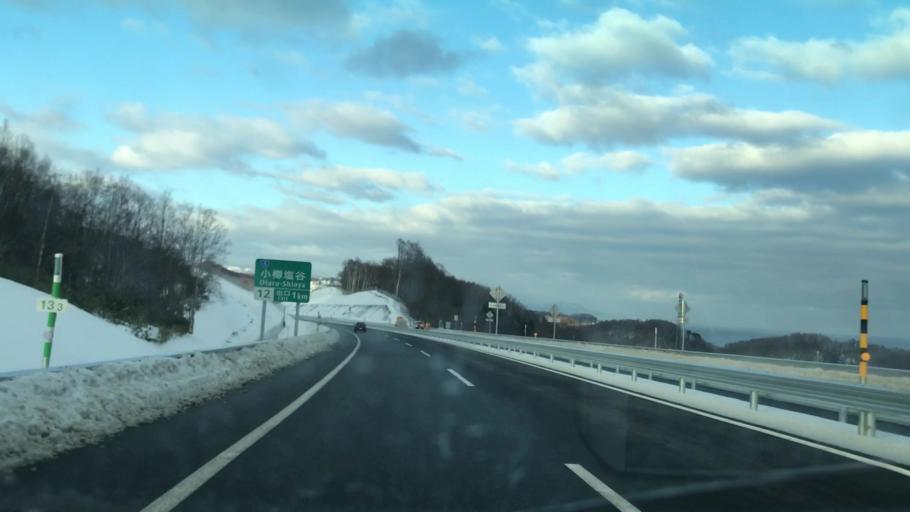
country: JP
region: Hokkaido
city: Otaru
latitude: 43.1997
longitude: 140.9416
